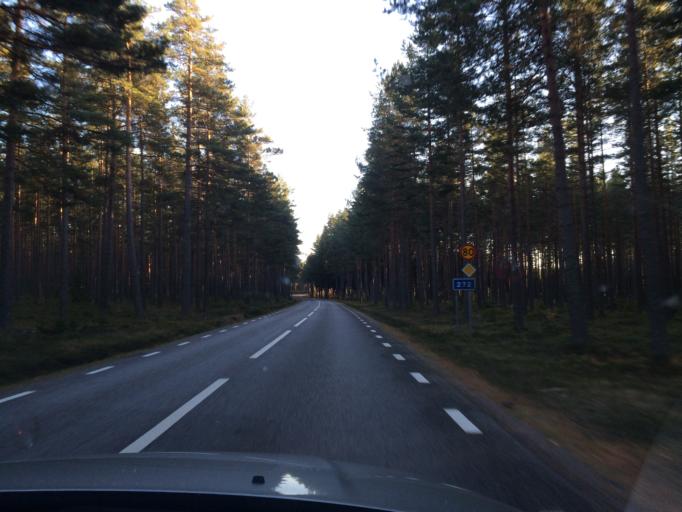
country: SE
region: Gaevleborg
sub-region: Sandvikens Kommun
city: Arsunda
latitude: 60.4935
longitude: 16.7234
